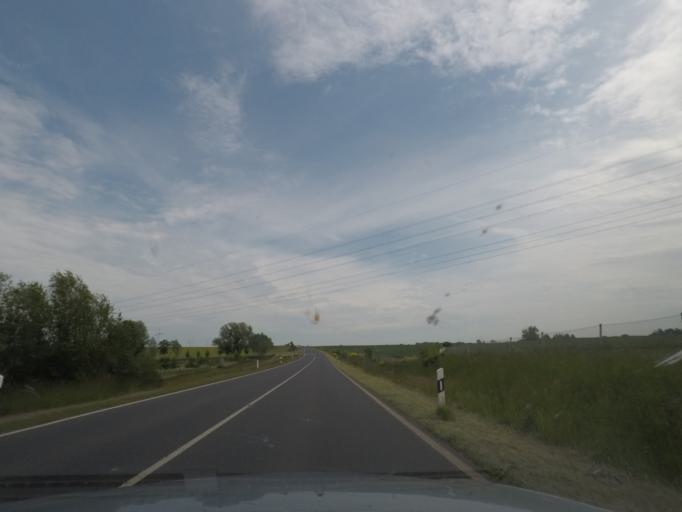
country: DE
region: Brandenburg
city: Schenkenberg
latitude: 53.3512
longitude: 13.9627
